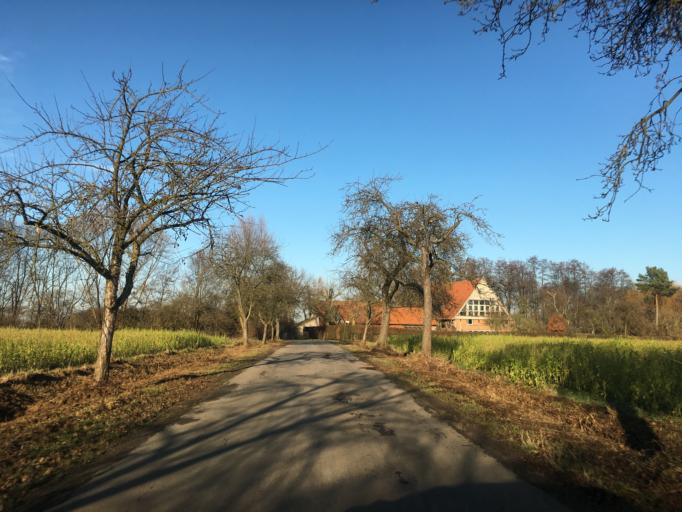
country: DE
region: North Rhine-Westphalia
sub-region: Regierungsbezirk Munster
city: Altenberge
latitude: 52.0389
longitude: 7.5222
